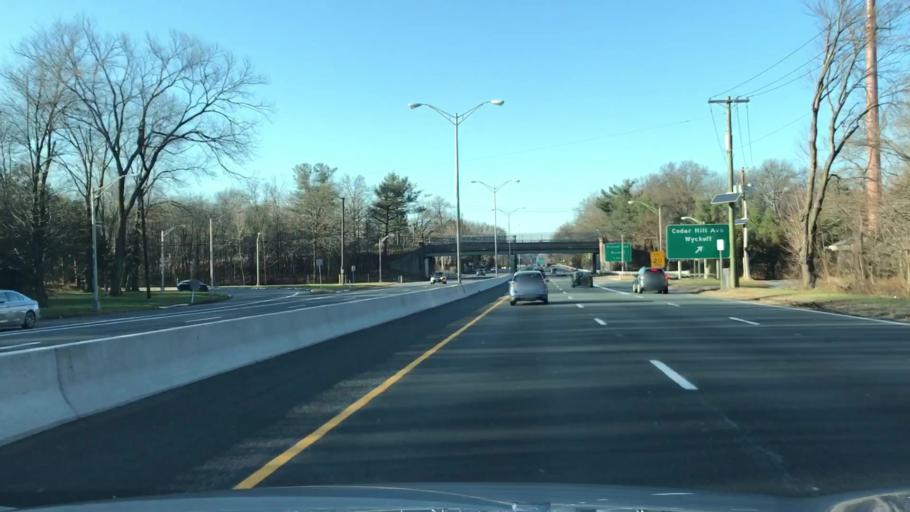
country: US
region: New Jersey
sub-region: Bergen County
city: Wyckoff
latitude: 40.9860
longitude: -74.1664
